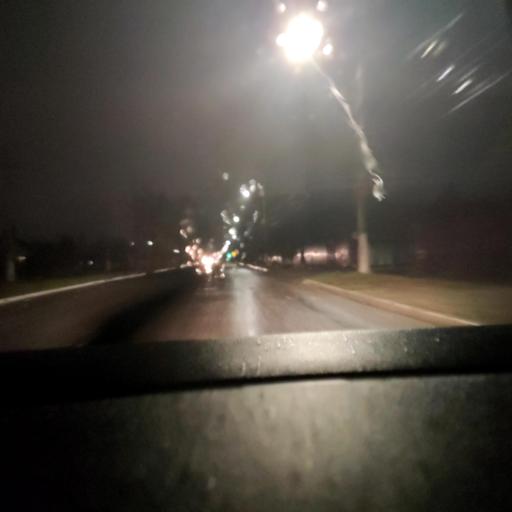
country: RU
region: Voronezj
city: Semiluki
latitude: 51.6933
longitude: 39.0333
